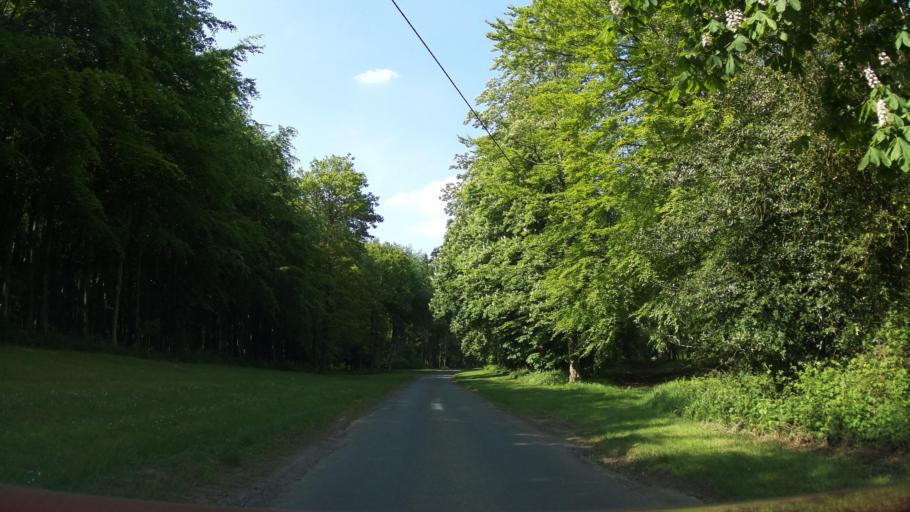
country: GB
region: England
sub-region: Wiltshire
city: Luckington
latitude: 51.5731
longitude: -2.2741
